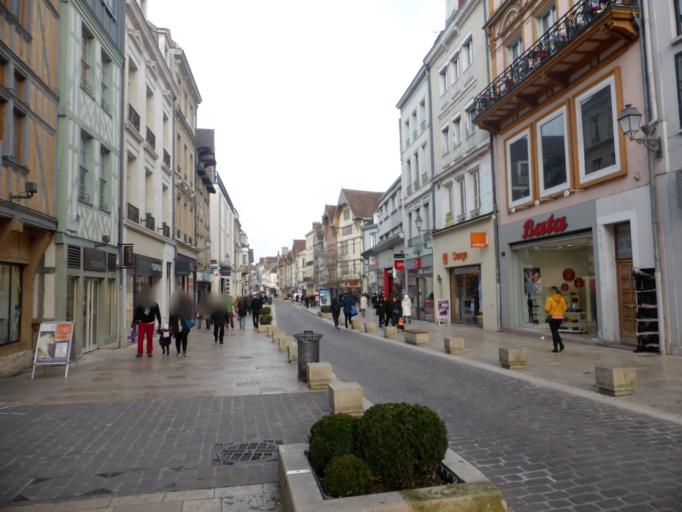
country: FR
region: Champagne-Ardenne
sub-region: Departement de l'Aube
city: Troyes
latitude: 48.2956
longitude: 4.0729
